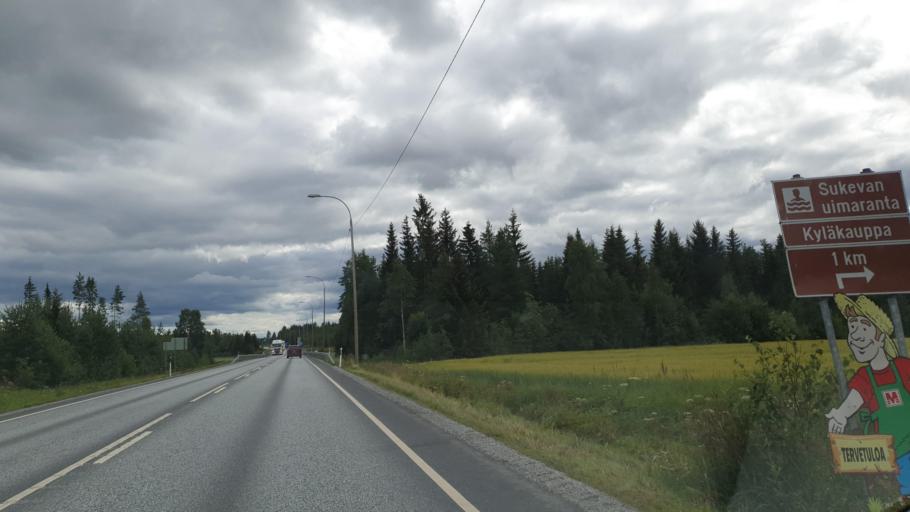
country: FI
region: Northern Savo
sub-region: Ylae-Savo
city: Sonkajaervi
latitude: 63.8778
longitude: 27.4408
